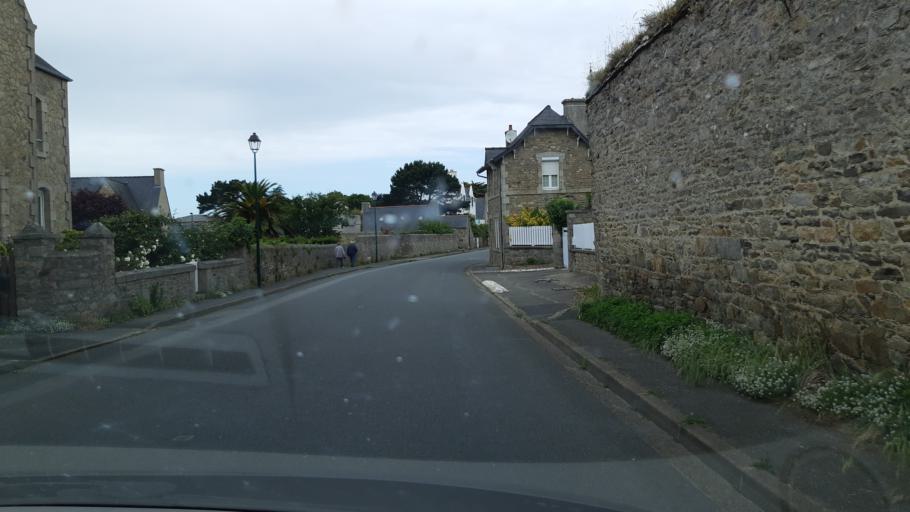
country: FR
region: Brittany
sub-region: Departement du Finistere
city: Roscoff
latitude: 48.7192
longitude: -3.9853
